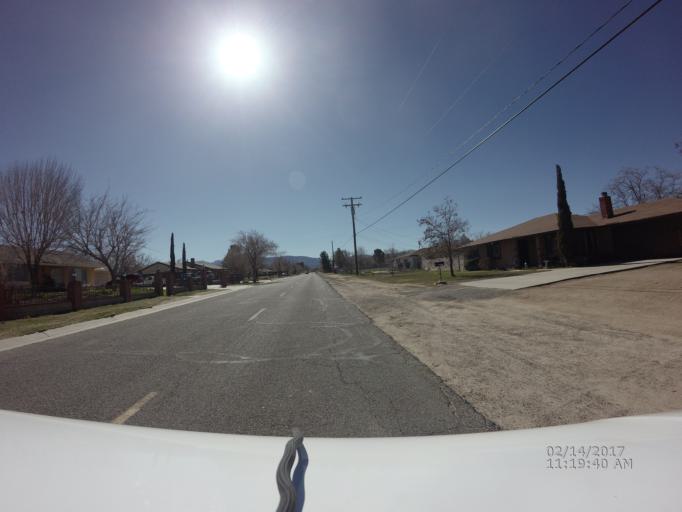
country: US
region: California
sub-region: Los Angeles County
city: Littlerock
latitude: 34.5627
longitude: -117.9608
